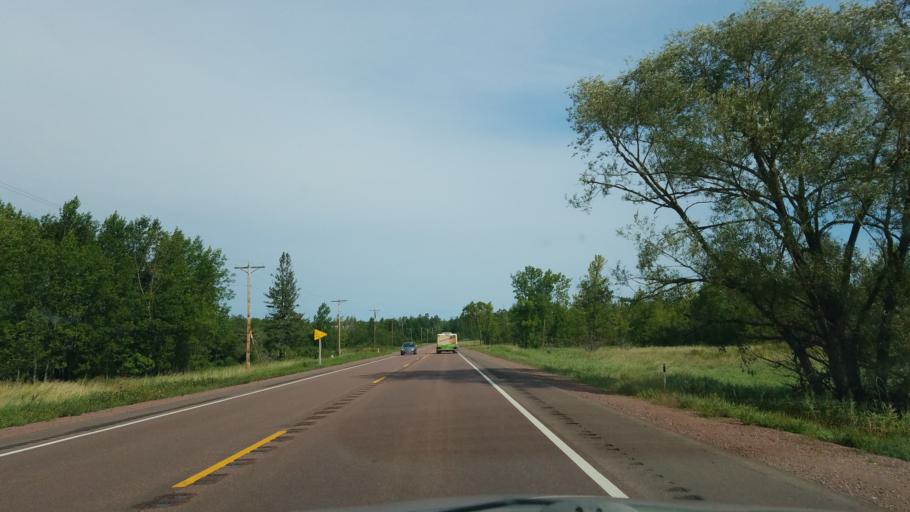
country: US
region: Wisconsin
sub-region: Ashland County
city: Ashland
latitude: 46.5967
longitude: -90.9551
